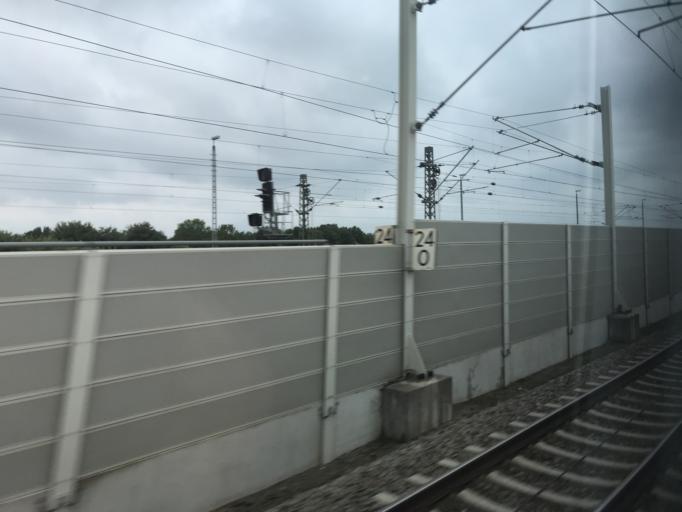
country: DE
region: Bavaria
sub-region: Upper Bavaria
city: Maisach
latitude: 48.2139
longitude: 11.2691
